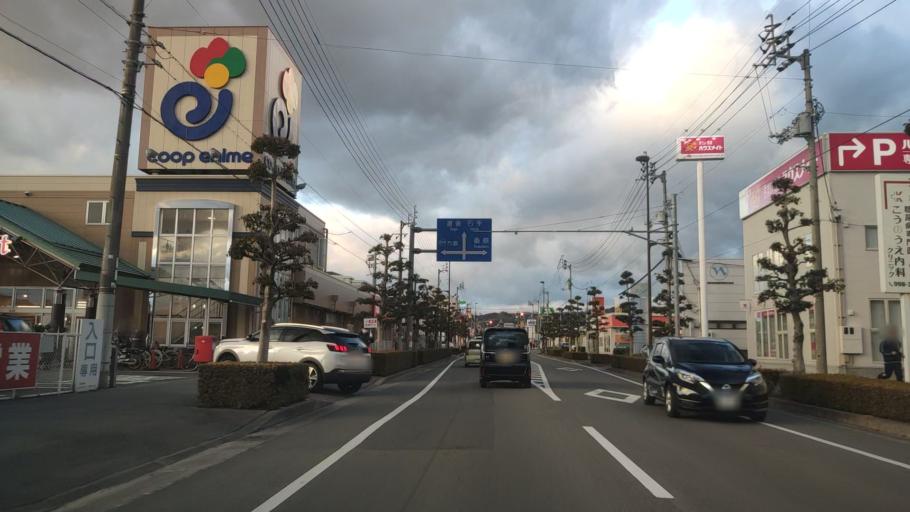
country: JP
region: Ehime
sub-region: Shikoku-chuo Shi
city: Matsuyama
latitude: 33.8318
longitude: 132.7874
